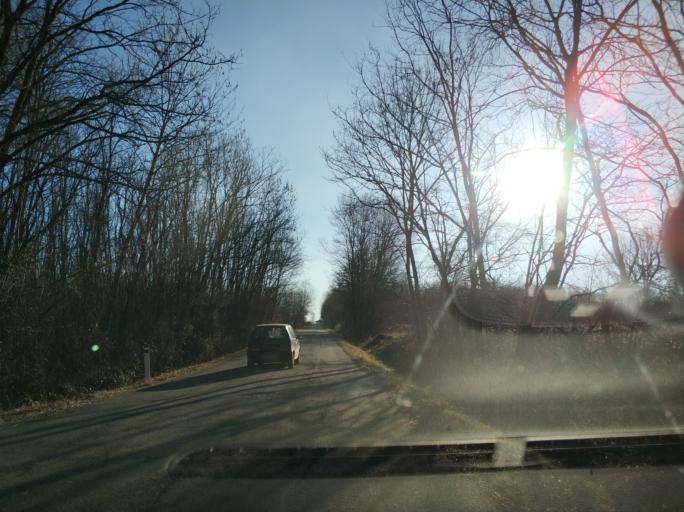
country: IT
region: Piedmont
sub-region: Provincia di Torino
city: Front
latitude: 45.2637
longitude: 7.6446
